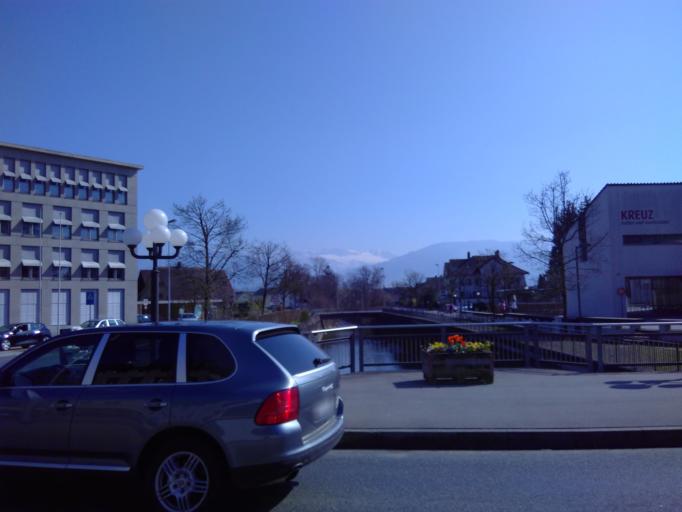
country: CH
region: Saint Gallen
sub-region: Wahlkreis See-Gaster
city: Jona
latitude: 47.2302
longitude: 8.8368
